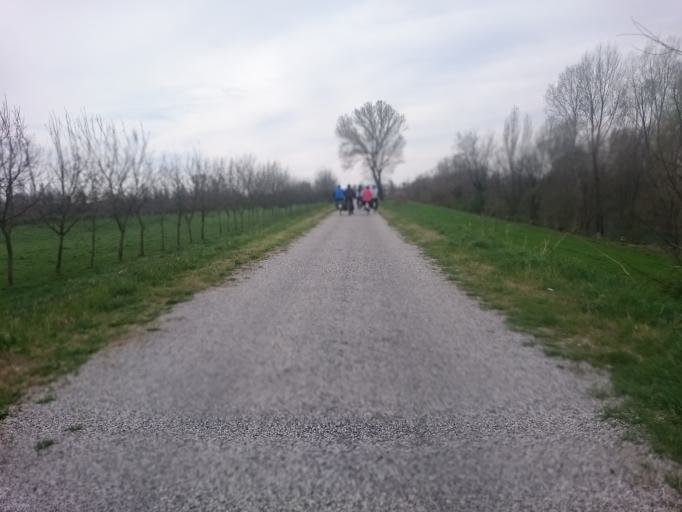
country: IT
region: Veneto
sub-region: Provincia di Padova
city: Saletto
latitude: 45.4757
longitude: 11.8530
